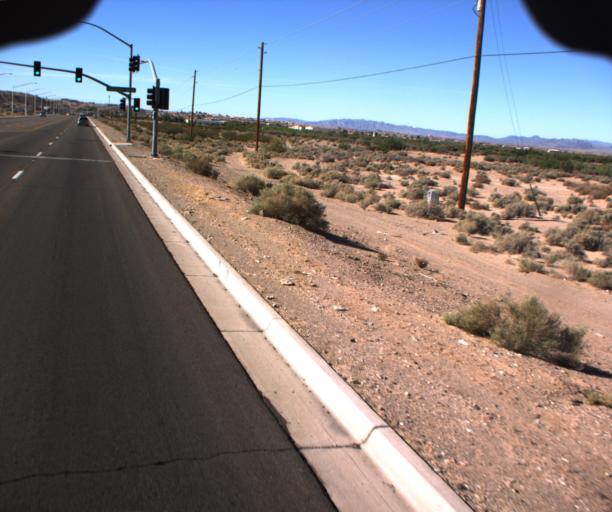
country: US
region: Arizona
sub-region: Mohave County
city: Bullhead City
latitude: 35.0629
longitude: -114.5893
